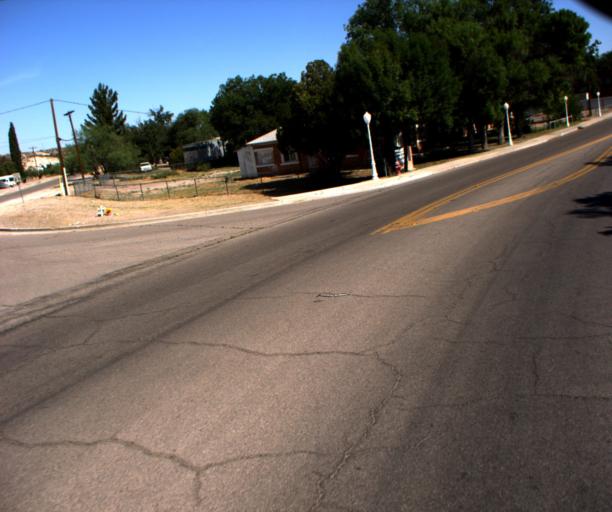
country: US
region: Arizona
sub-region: Greenlee County
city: Clifton
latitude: 32.7175
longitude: -109.1028
